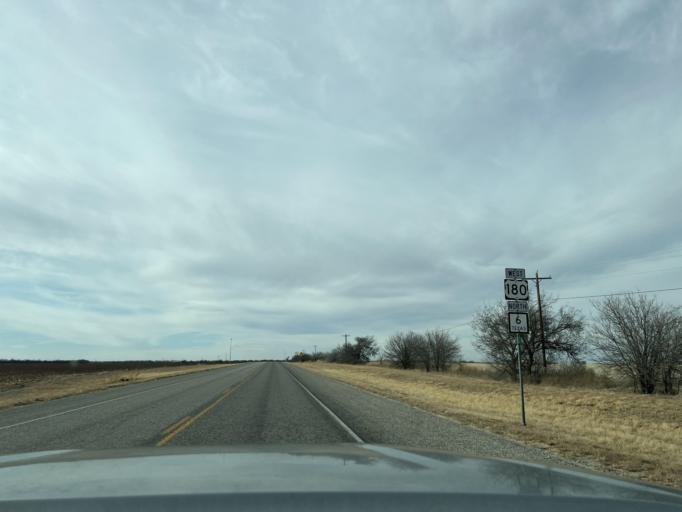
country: US
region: Texas
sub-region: Jones County
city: Stamford
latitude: 32.7649
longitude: -99.5814
